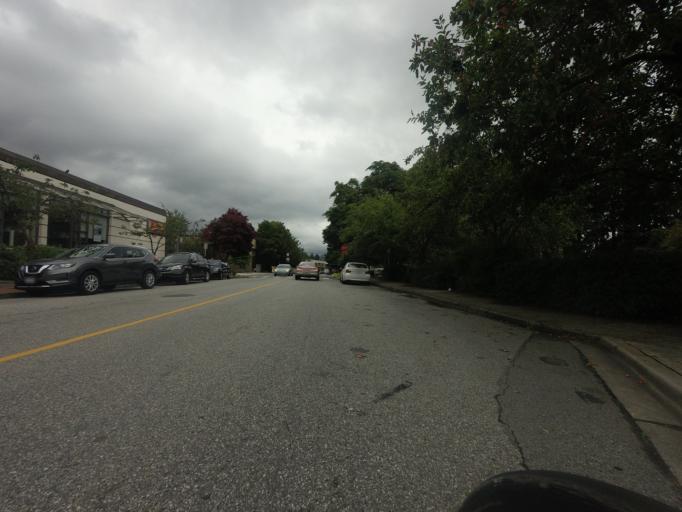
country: CA
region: British Columbia
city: West Vancouver
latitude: 49.3277
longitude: -123.1607
